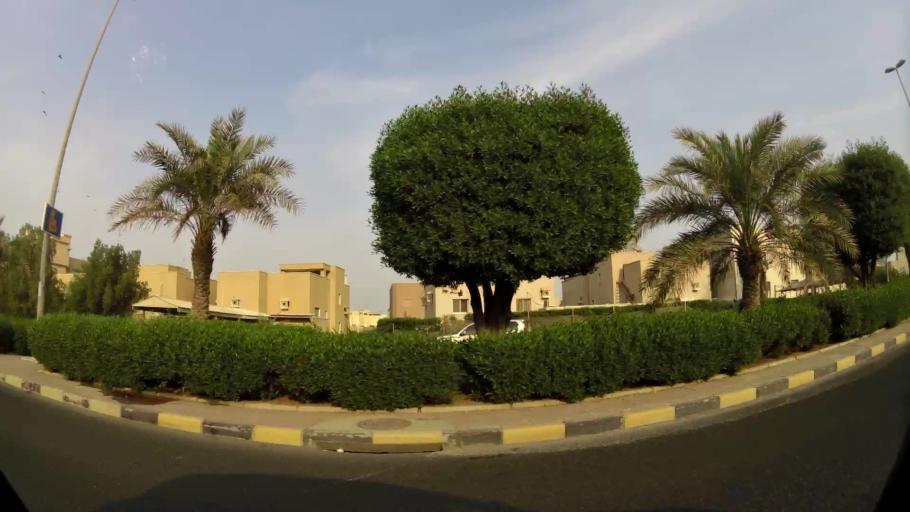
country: KW
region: Mubarak al Kabir
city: Mubarak al Kabir
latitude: 29.1952
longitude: 48.0687
